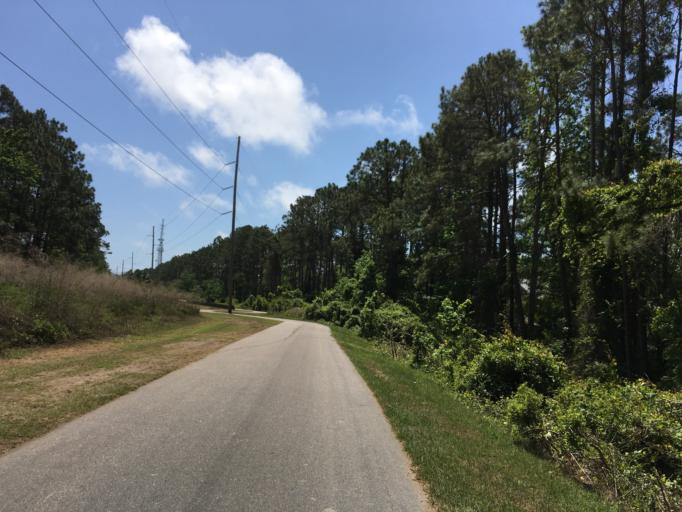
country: US
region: South Carolina
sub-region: Beaufort County
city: Hilton Head Island
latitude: 32.1668
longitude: -80.7673
